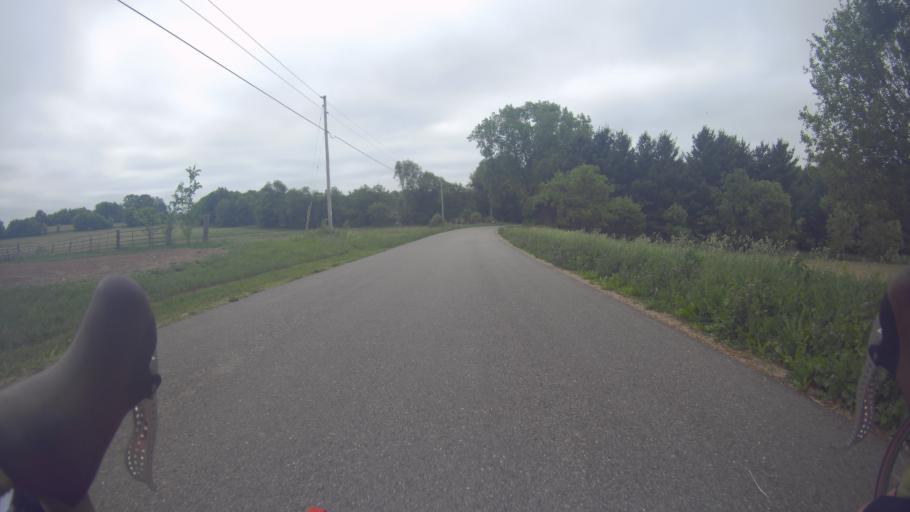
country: US
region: Wisconsin
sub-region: Green County
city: Brooklyn
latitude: 42.8754
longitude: -89.3602
